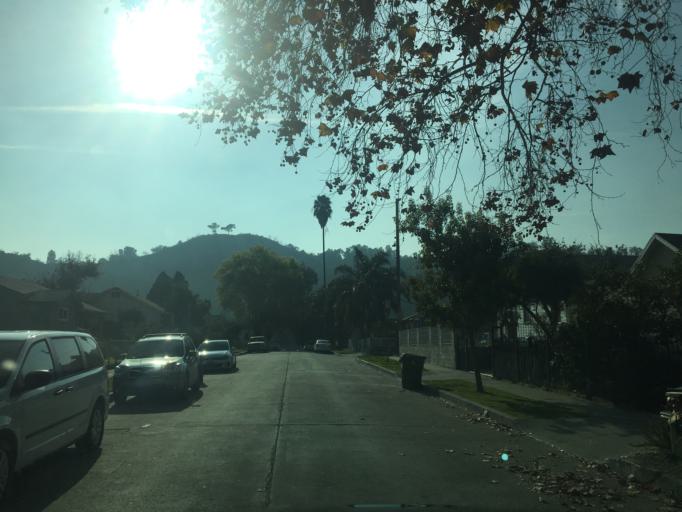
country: US
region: California
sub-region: Los Angeles County
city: Echo Park
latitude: 34.0897
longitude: -118.2307
